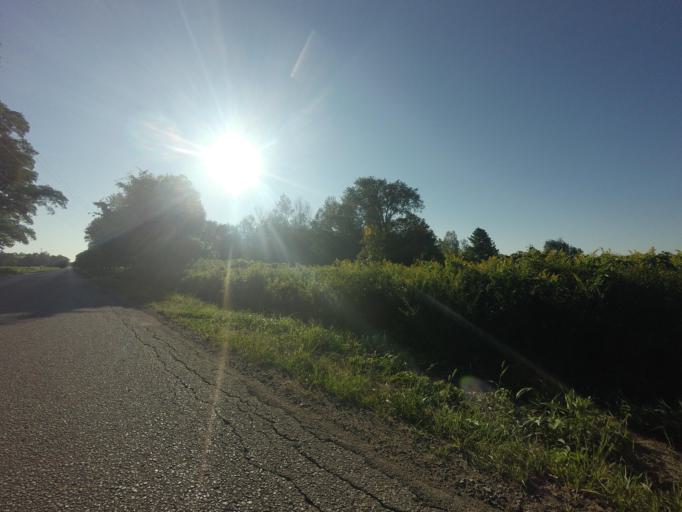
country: CA
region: Ontario
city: Bradford West Gwillimbury
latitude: 44.0456
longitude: -79.7581
